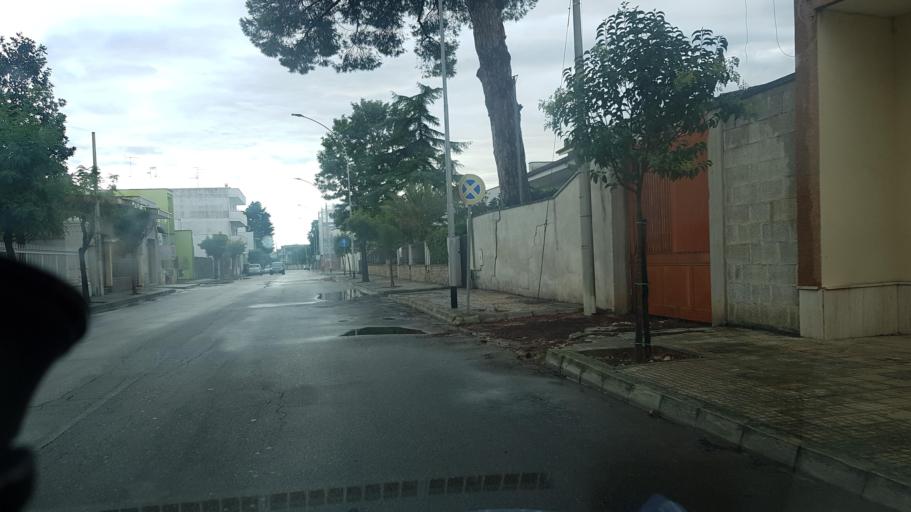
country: IT
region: Apulia
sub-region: Provincia di Lecce
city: Carmiano
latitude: 40.3437
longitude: 18.0490
